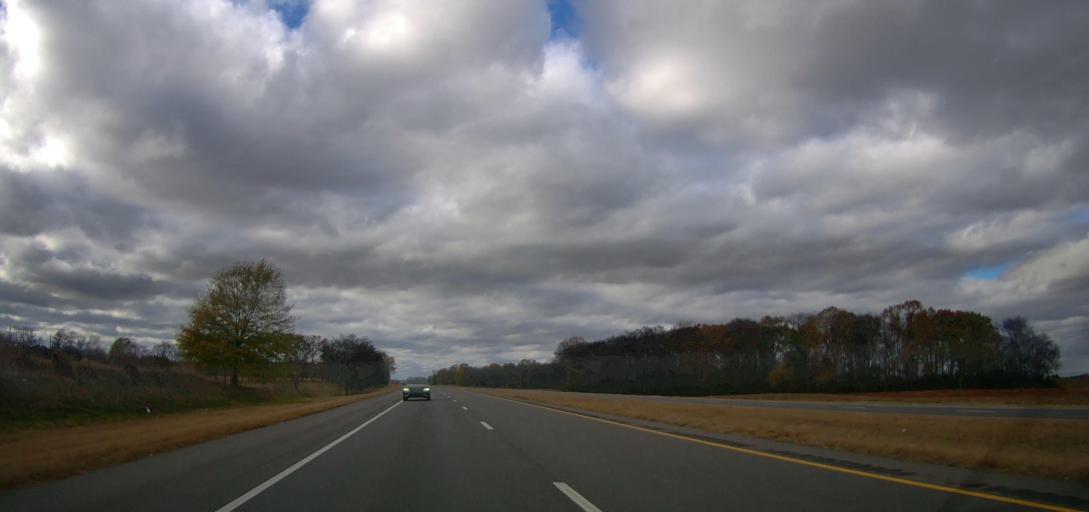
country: US
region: Alabama
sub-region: Lawrence County
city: Moulton
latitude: 34.4573
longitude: -87.2365
